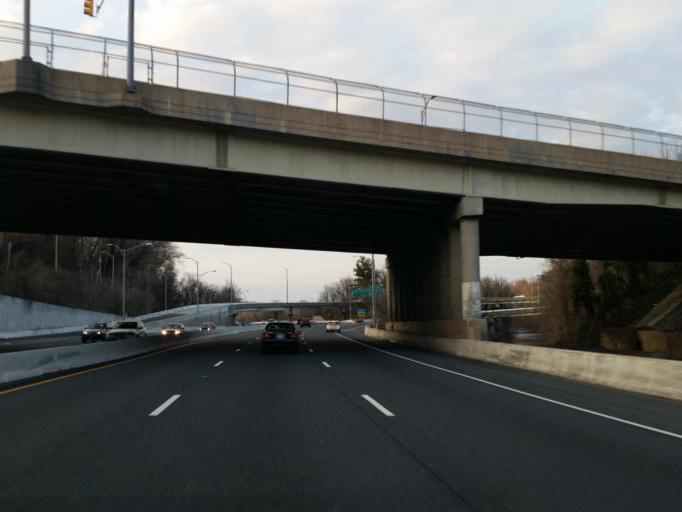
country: US
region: Maryland
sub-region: Baltimore County
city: Towson
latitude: 39.3601
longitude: -76.6503
